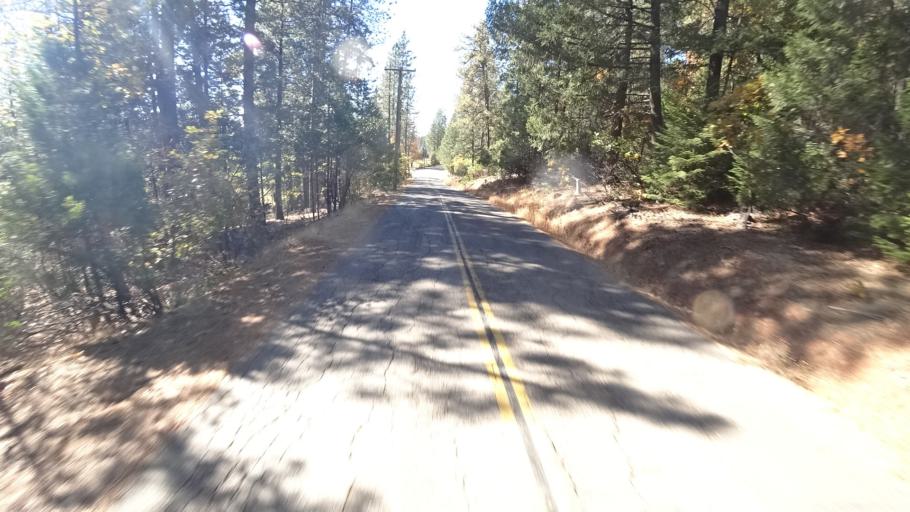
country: US
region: California
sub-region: Shasta County
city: Shingletown
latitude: 40.7193
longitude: -121.9349
